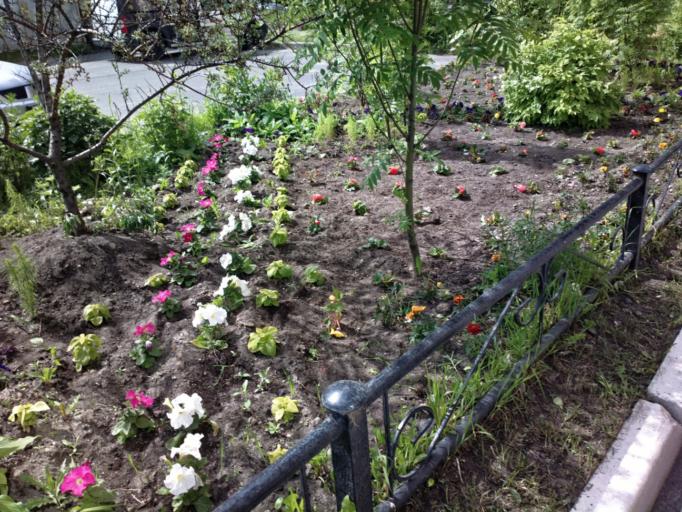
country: RU
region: St.-Petersburg
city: Vasyl'evsky Ostrov
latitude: 59.9409
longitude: 30.2131
